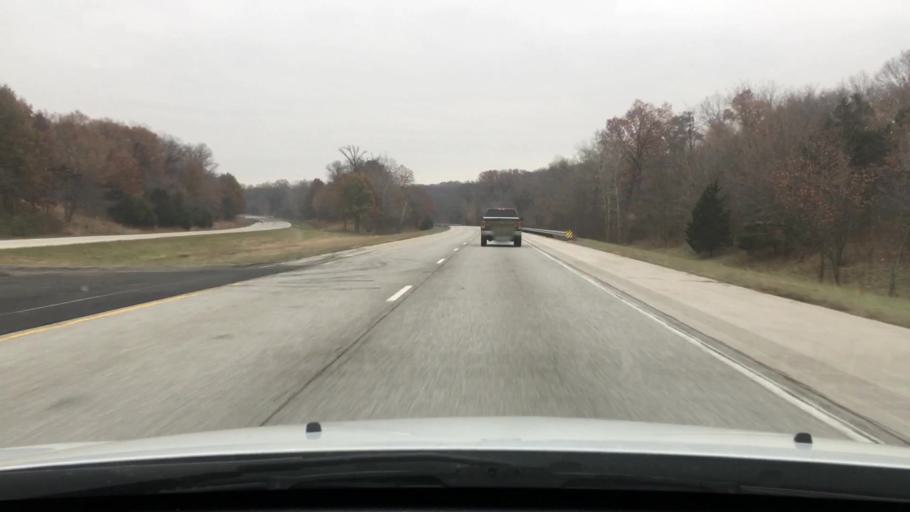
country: US
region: Illinois
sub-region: Pike County
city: Griggsville
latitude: 39.6811
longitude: -90.6645
